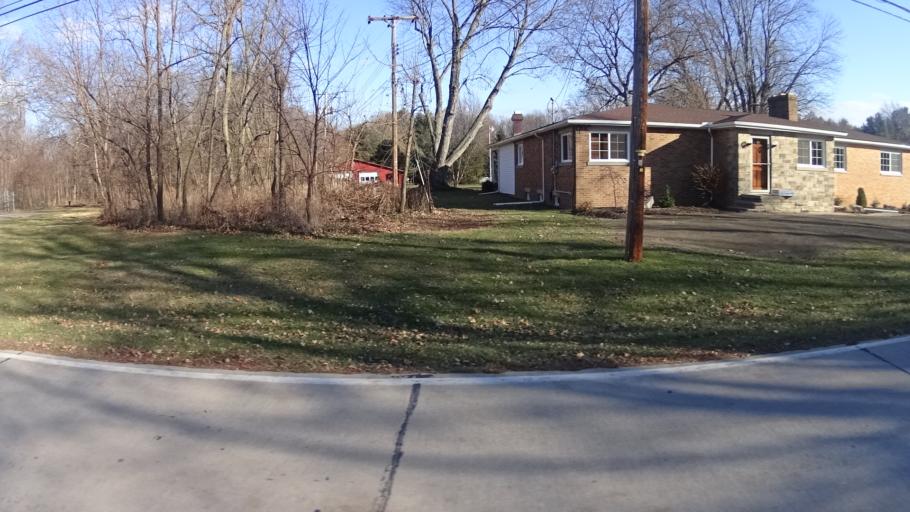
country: US
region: Ohio
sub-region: Lorain County
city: North Ridgeville
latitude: 41.3859
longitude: -82.0320
